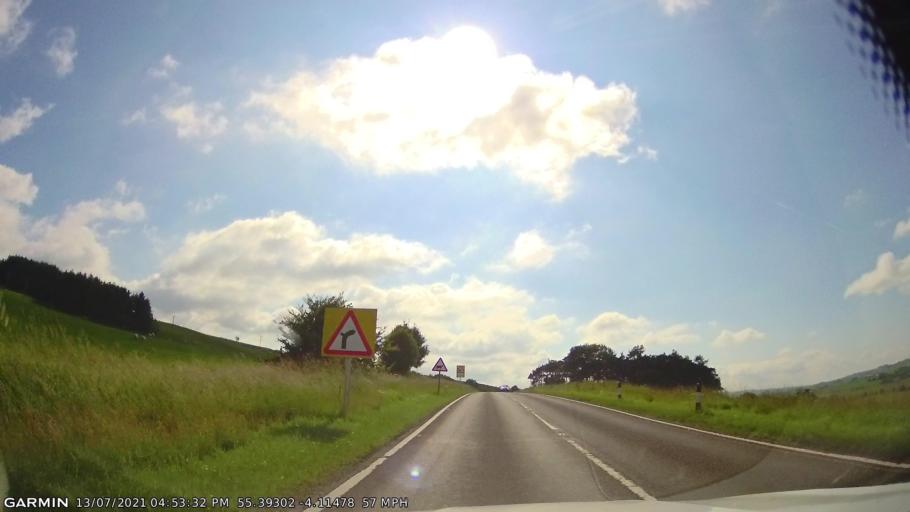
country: GB
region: Scotland
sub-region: East Ayrshire
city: New Cumnock
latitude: 55.3931
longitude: -4.1144
